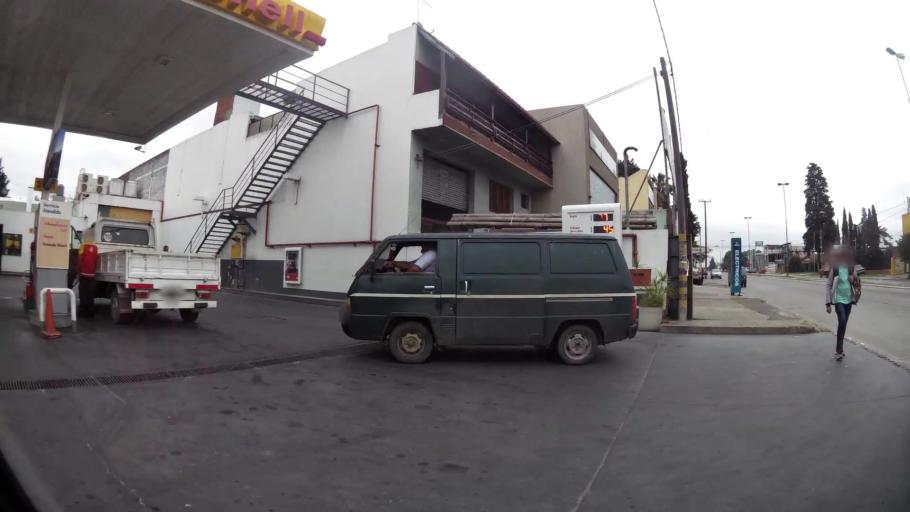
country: AR
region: Buenos Aires
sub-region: Partido de La Plata
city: La Plata
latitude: -34.9452
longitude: -57.9929
